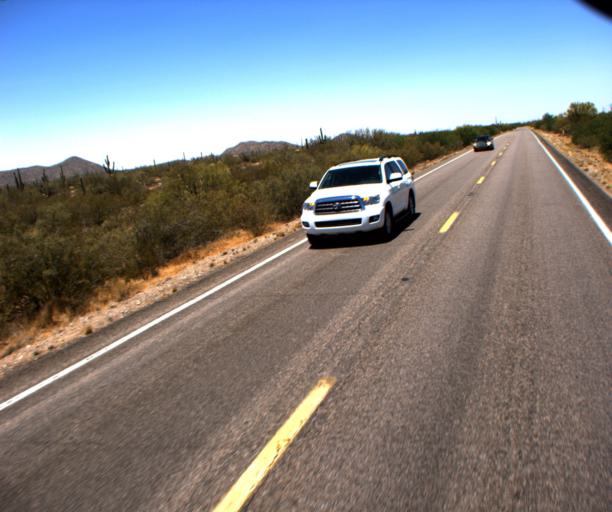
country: US
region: Arizona
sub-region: Pima County
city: Catalina
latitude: 32.7160
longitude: -111.1040
